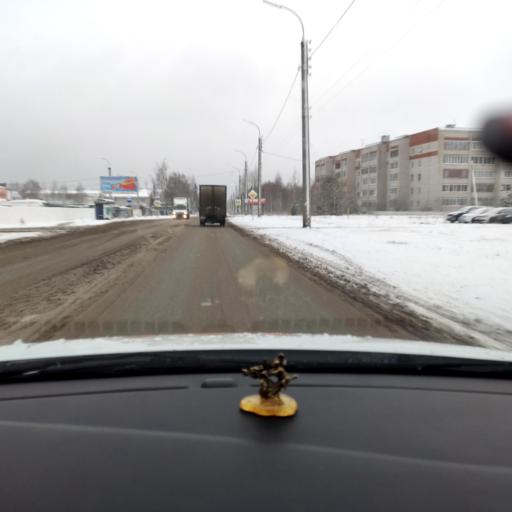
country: RU
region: Tatarstan
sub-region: Zelenodol'skiy Rayon
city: Zelenodolsk
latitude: 55.8620
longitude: 48.5506
